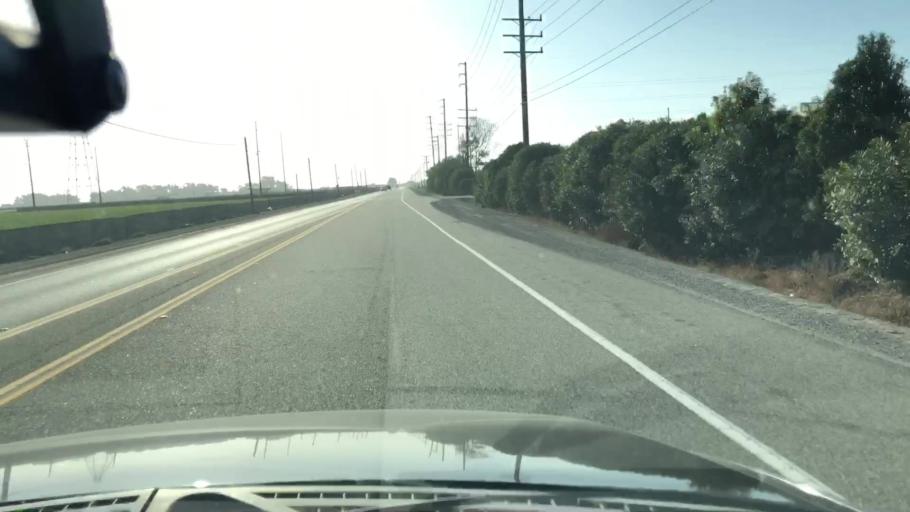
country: US
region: California
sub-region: Ventura County
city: Oxnard Shores
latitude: 34.2195
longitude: -119.2270
